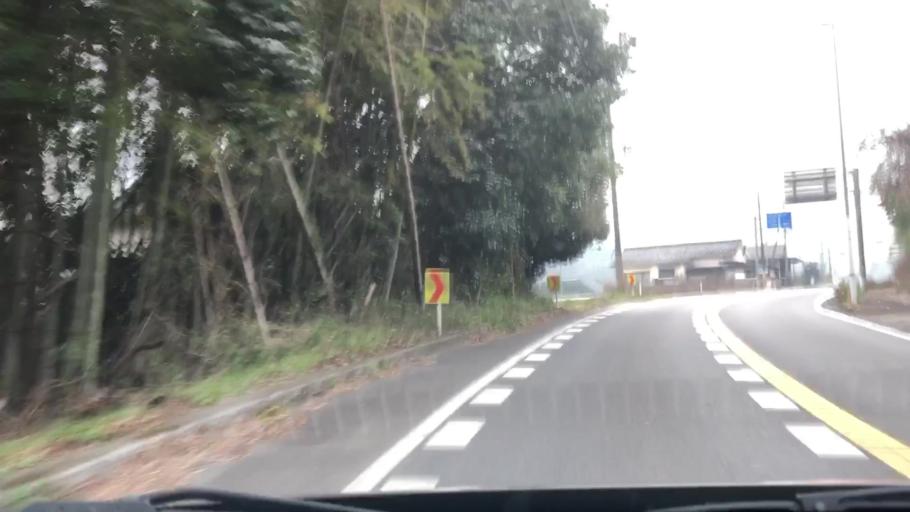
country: JP
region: Oita
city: Usuki
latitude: 33.0303
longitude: 131.6936
